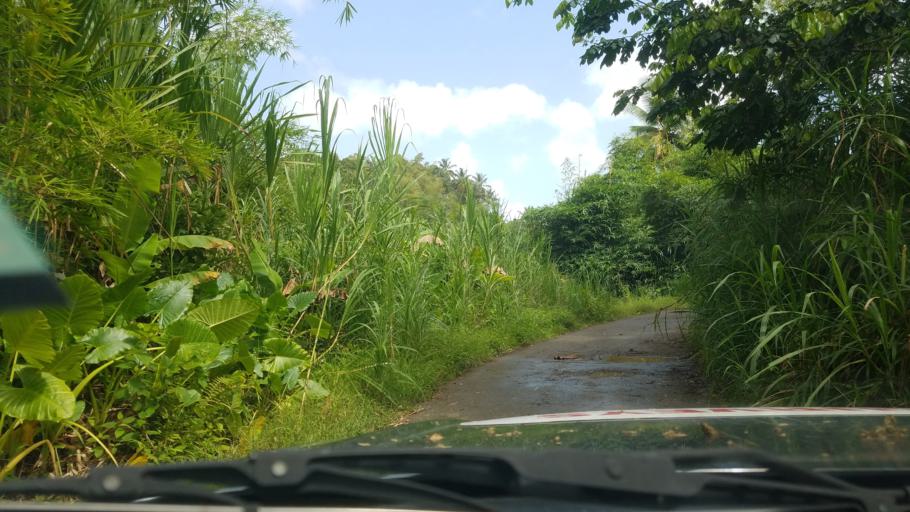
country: LC
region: Anse-la-Raye
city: Anse La Raye
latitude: 13.9421
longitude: -60.9901
